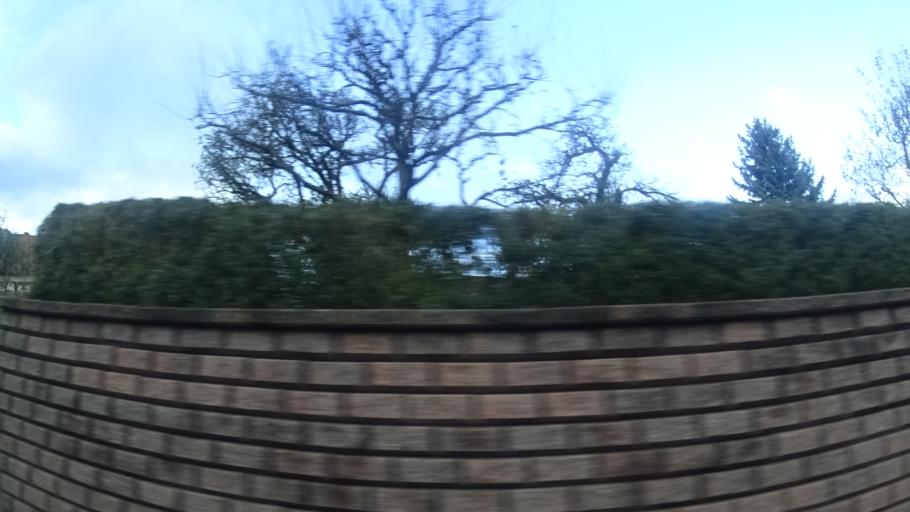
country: DE
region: Hesse
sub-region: Regierungsbezirk Kassel
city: Flieden
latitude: 50.4517
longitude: 9.5725
